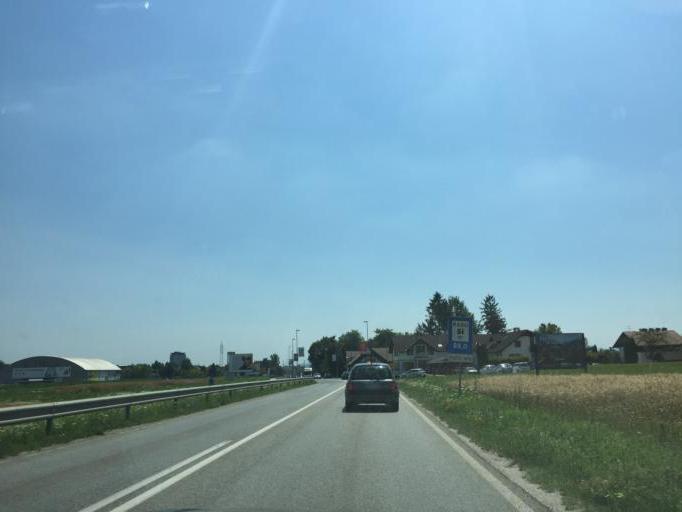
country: SI
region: Kranj
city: Kranj
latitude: 46.2526
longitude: 14.3434
